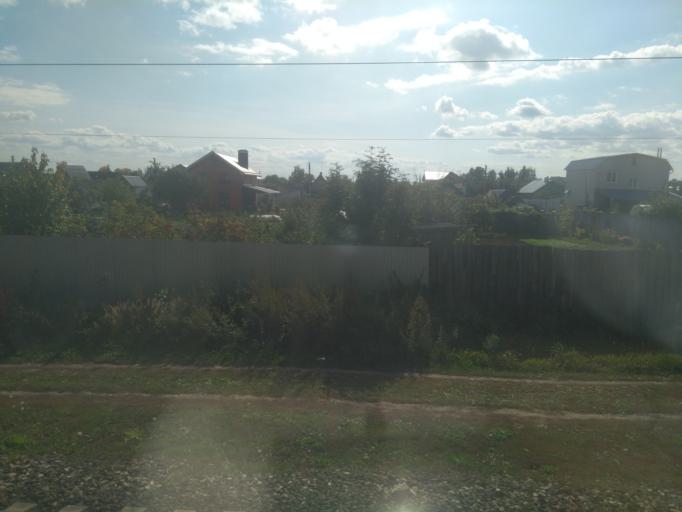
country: RU
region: Tatarstan
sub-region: Zelenodol'skiy Rayon
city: Zelenodolsk
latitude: 55.8419
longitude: 48.5694
